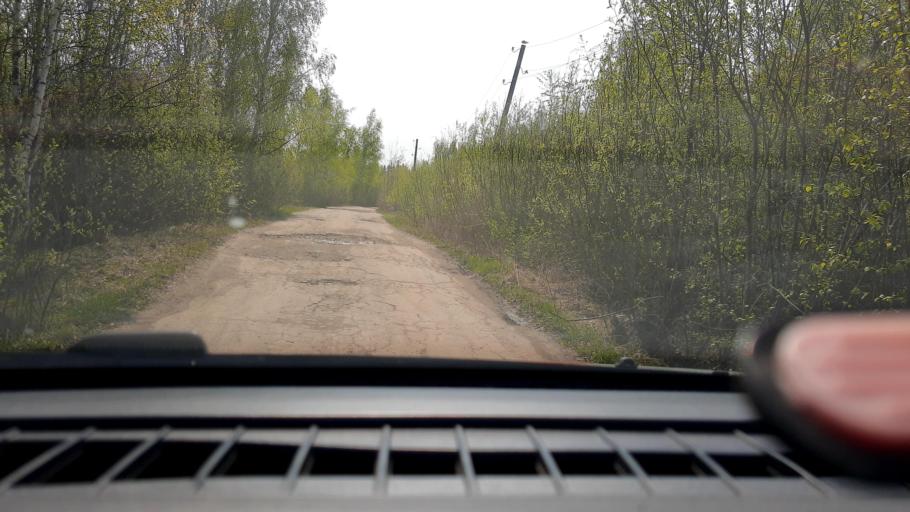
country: RU
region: Nizjnij Novgorod
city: Gorbatovka
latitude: 56.2701
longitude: 43.7973
